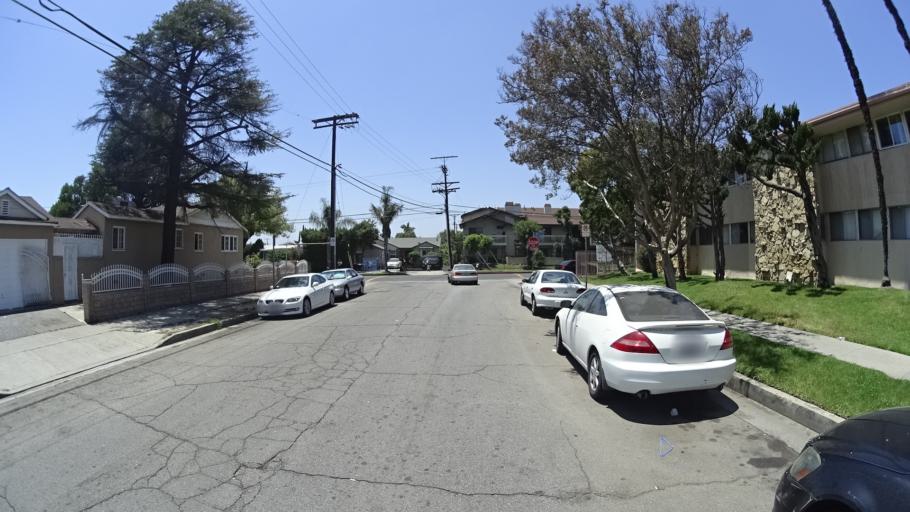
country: US
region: California
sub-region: Los Angeles County
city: Van Nuys
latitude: 34.2198
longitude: -118.4550
